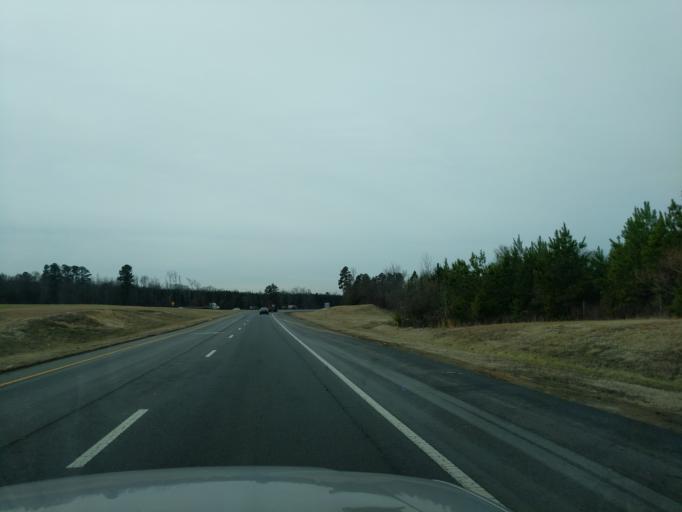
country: US
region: North Carolina
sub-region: Mecklenburg County
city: Huntersville
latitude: 35.3653
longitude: -80.8450
